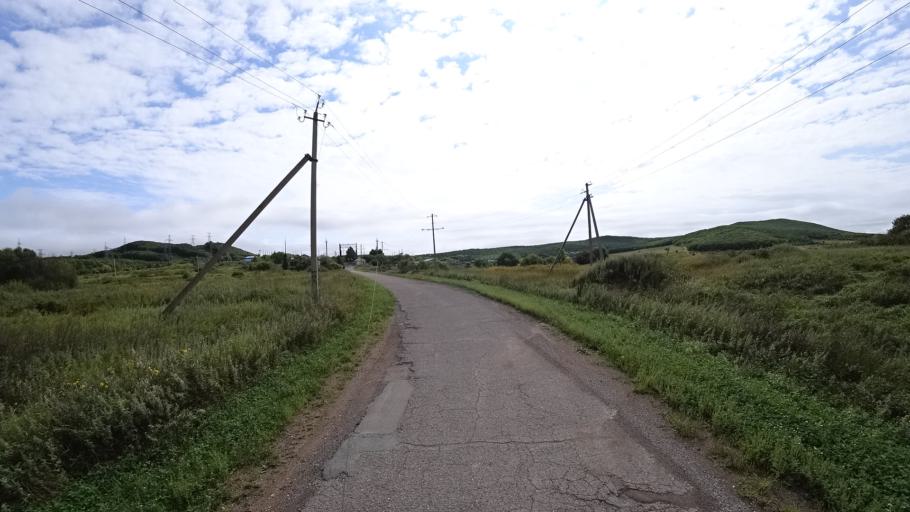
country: RU
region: Primorskiy
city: Lyalichi
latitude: 44.1324
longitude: 132.3877
